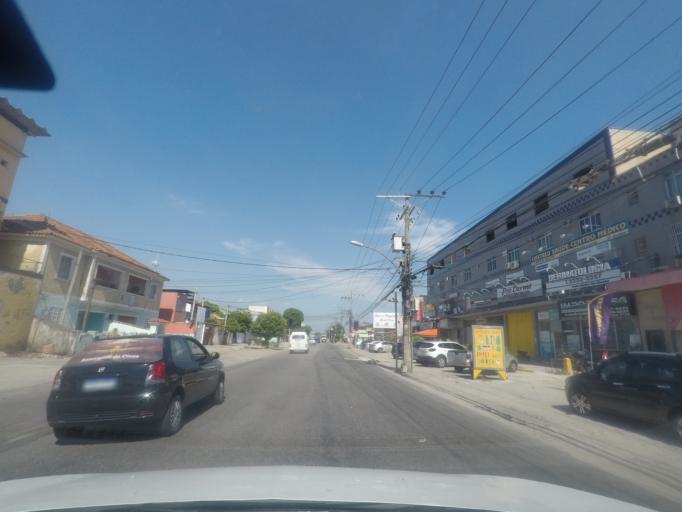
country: BR
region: Rio de Janeiro
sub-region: Nilopolis
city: Nilopolis
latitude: -22.8796
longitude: -43.4560
